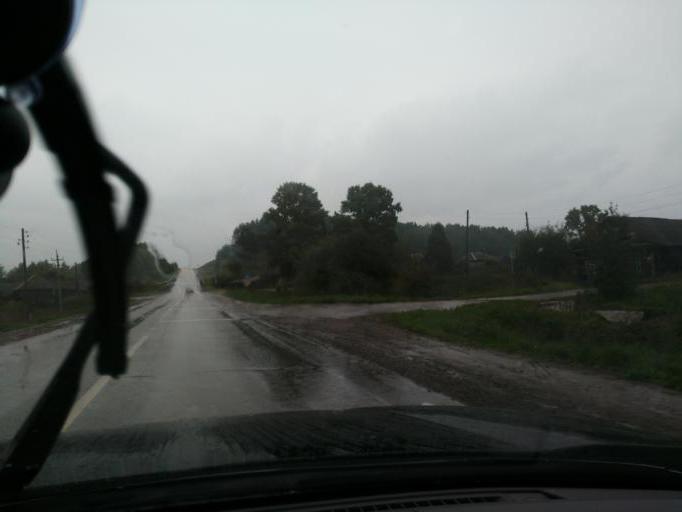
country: RU
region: Perm
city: Osa
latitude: 57.1884
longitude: 55.5910
